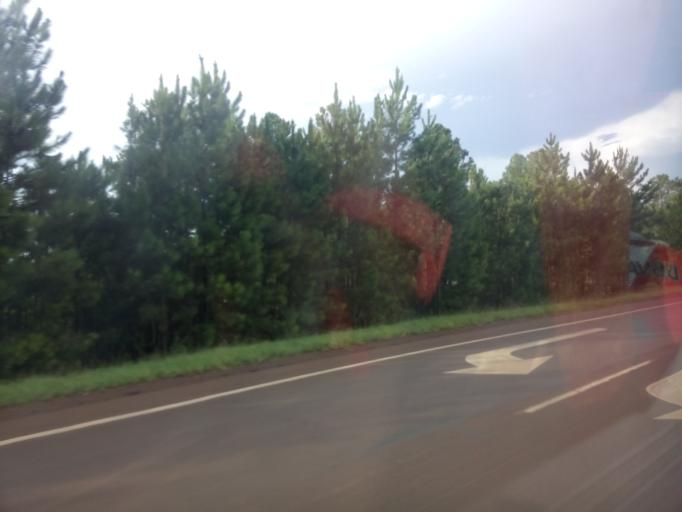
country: AR
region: Misiones
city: Santa Ana
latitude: -27.3896
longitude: -55.5970
